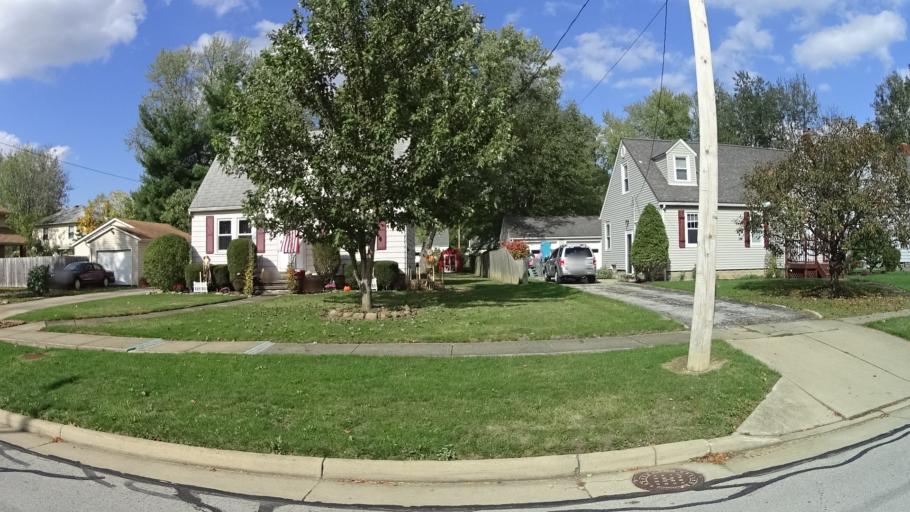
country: US
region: Ohio
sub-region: Lorain County
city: Grafton
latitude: 41.2700
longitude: -82.0507
